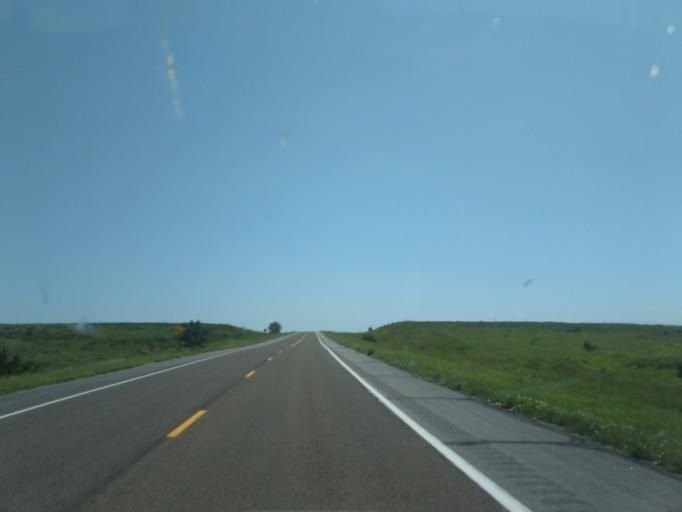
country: US
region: Nebraska
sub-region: Hitchcock County
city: Trenton
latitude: 40.1763
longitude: -101.1317
